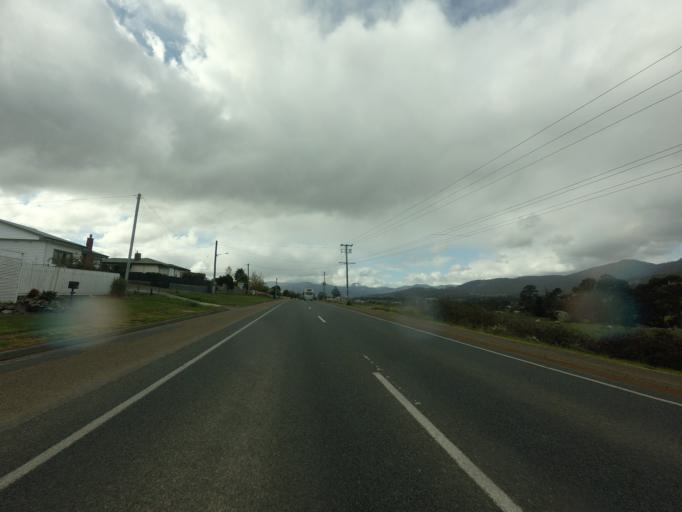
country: AU
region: Tasmania
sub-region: Huon Valley
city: Huonville
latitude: -43.0404
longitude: 147.0451
